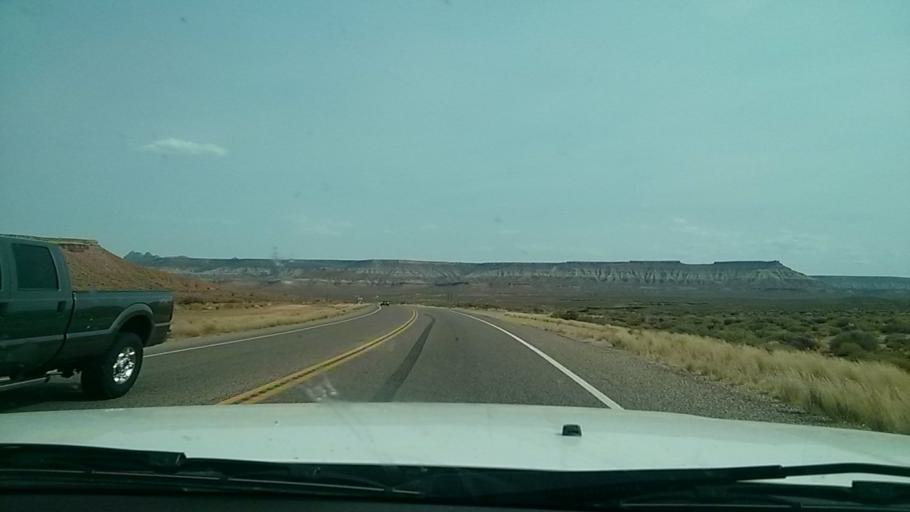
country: US
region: Utah
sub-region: Washington County
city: LaVerkin
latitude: 37.2186
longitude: -113.2501
